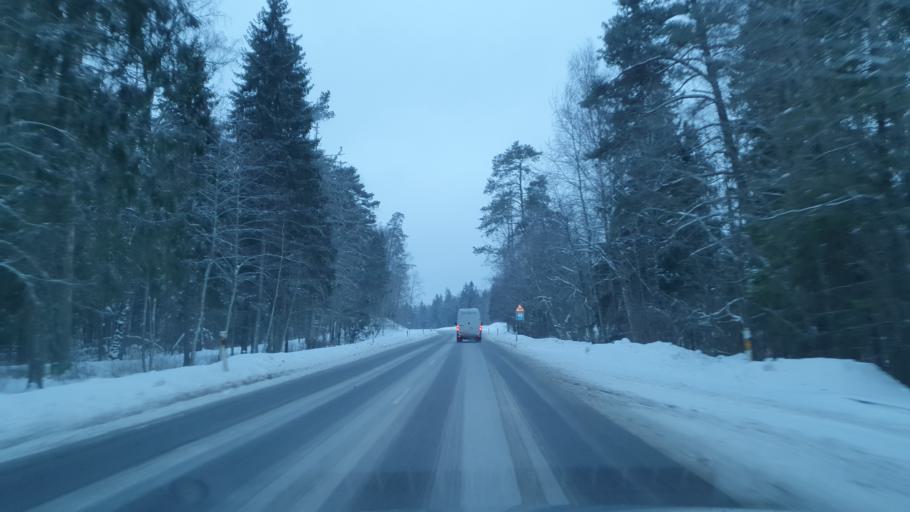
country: EE
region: Harju
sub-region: Kuusalu vald
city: Kuusalu
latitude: 59.2703
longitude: 25.6502
